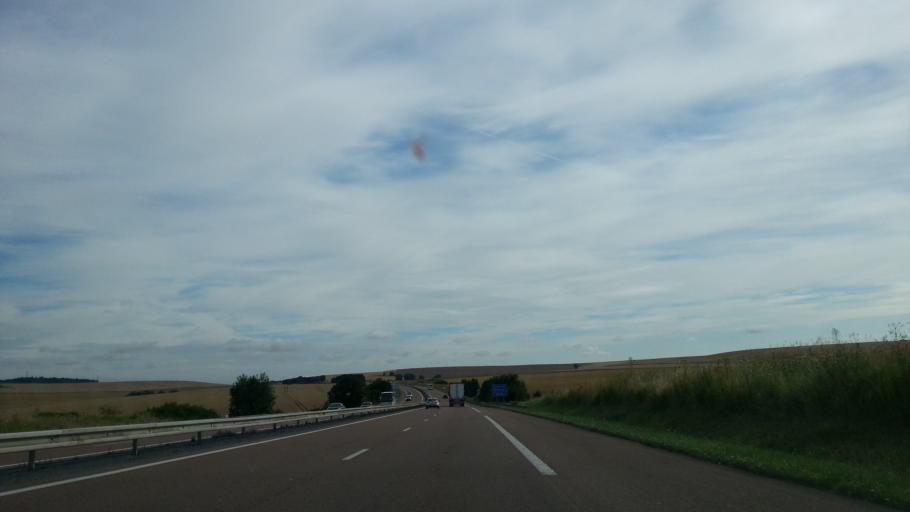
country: FR
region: Champagne-Ardenne
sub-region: Departement de la Marne
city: Chatillon-sur-Marne
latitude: 49.1689
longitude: 3.7402
